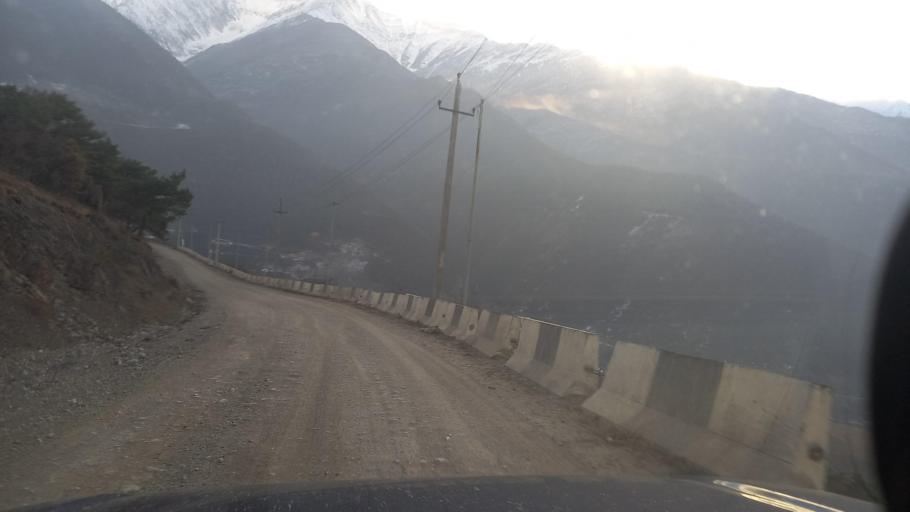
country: RU
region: Ingushetiya
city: Dzhayrakh
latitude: 42.8229
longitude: 44.7047
